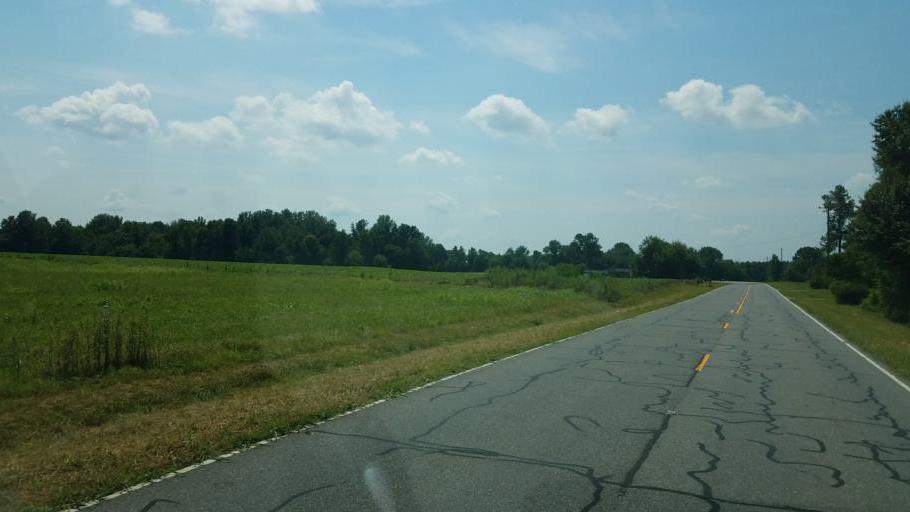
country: US
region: North Carolina
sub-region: Gaston County
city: Cherryville
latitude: 35.4602
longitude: -81.4344
